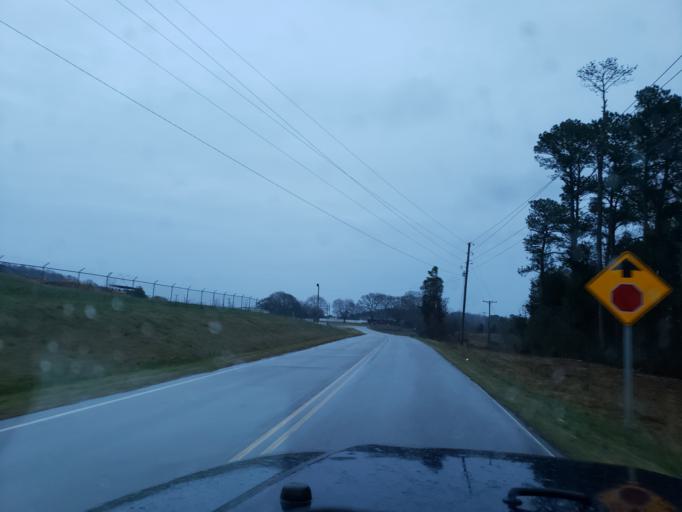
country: US
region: South Carolina
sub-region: Cherokee County
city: Blacksburg
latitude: 35.1563
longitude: -81.4541
